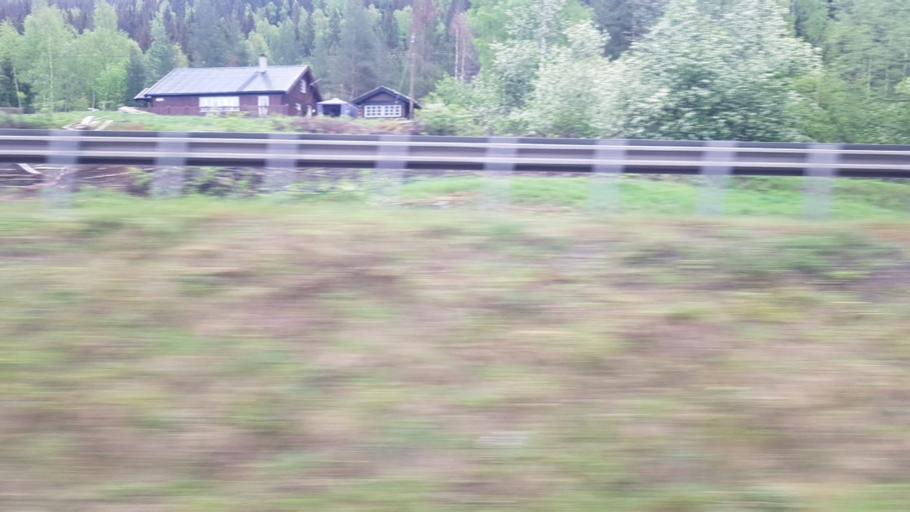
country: NO
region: Oppland
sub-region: Nord-Fron
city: Vinstra
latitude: 61.6242
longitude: 9.7159
